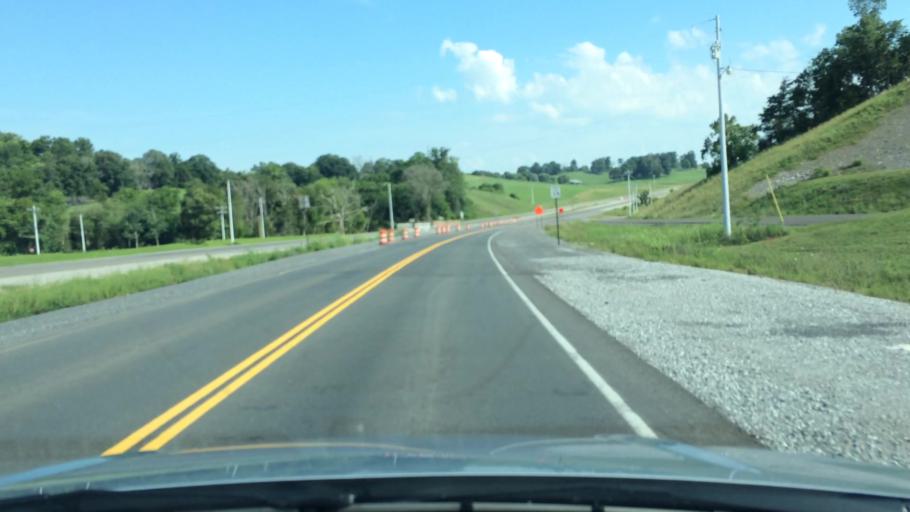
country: US
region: Tennessee
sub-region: Jefferson County
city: White Pine
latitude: 36.1404
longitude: -83.3432
